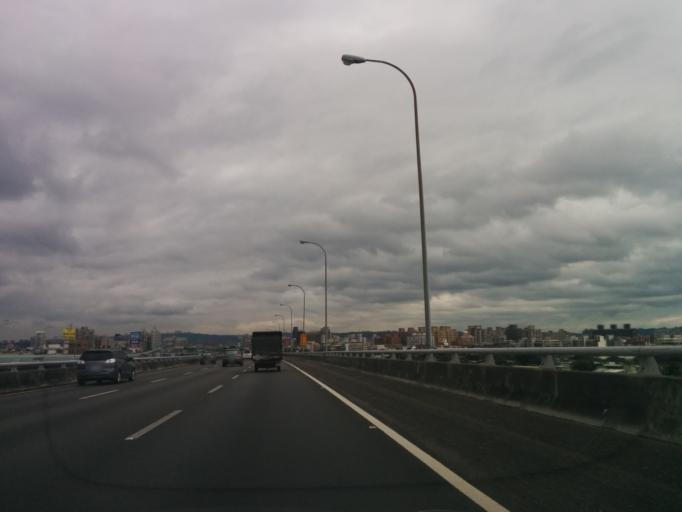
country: TW
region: Taipei
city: Taipei
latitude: 25.0781
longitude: 121.5030
